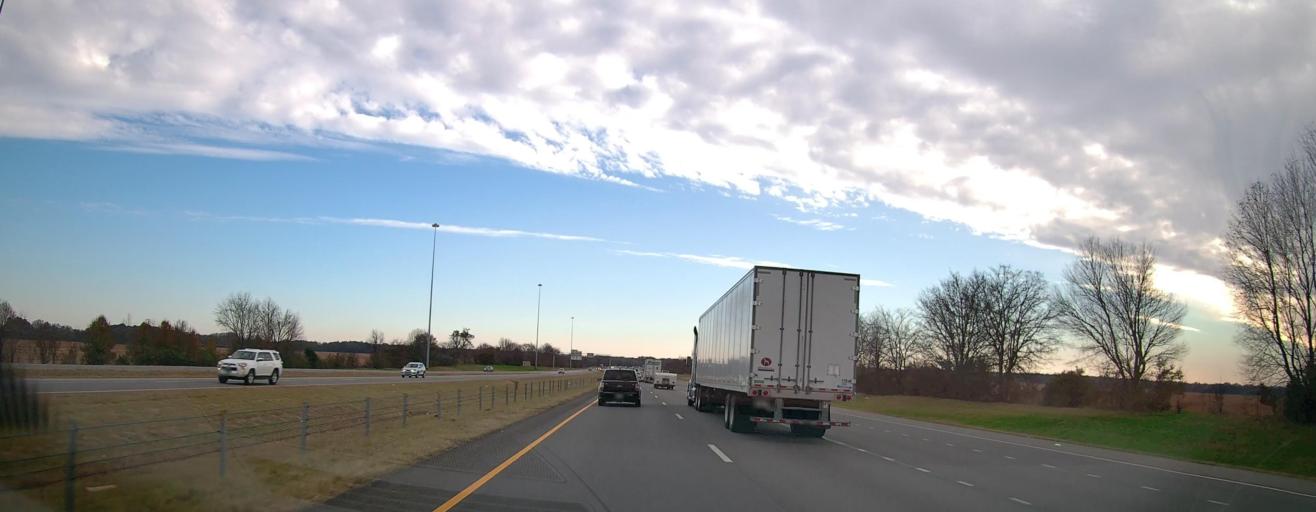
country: US
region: Alabama
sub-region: Morgan County
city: Decatur
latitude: 34.6229
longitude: -86.9006
